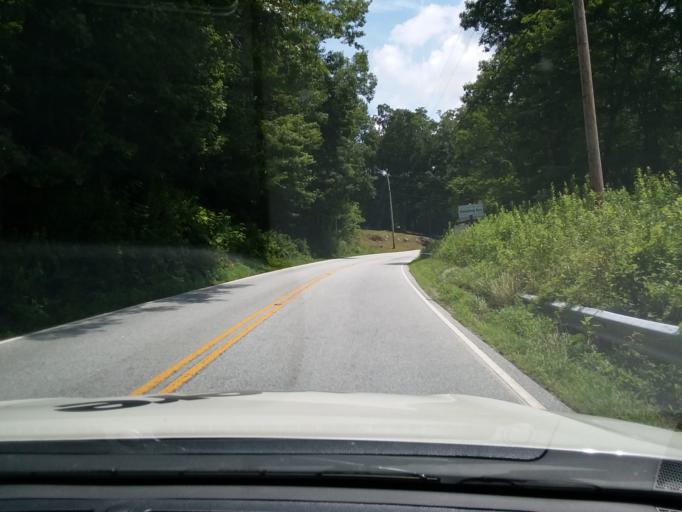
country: US
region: Georgia
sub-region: Rabun County
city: Mountain City
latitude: 35.0106
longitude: -83.3209
